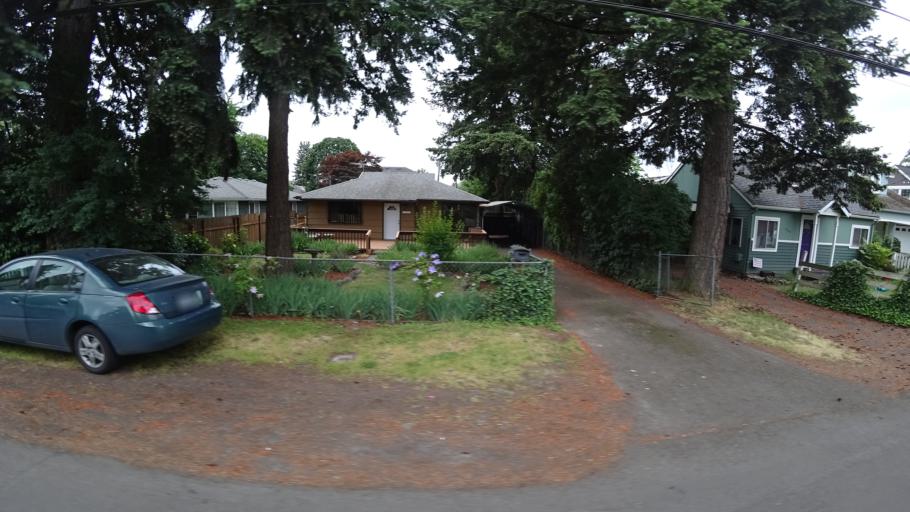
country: US
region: Oregon
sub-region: Multnomah County
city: Lents
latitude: 45.4710
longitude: -122.5874
